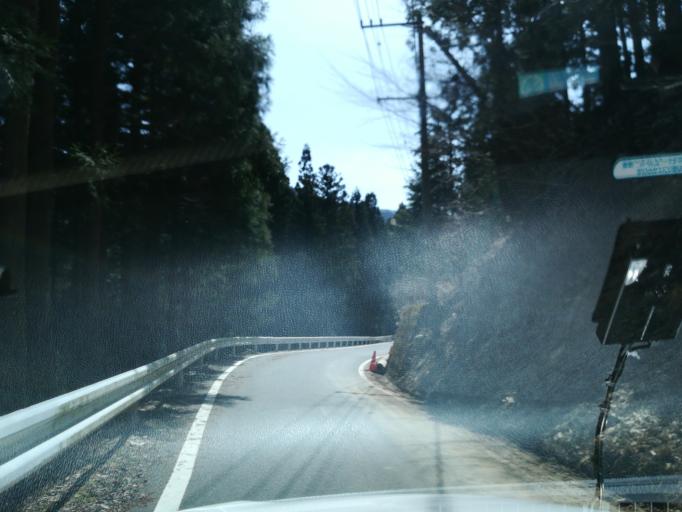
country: JP
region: Tokushima
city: Wakimachi
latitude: 33.8665
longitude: 134.0717
